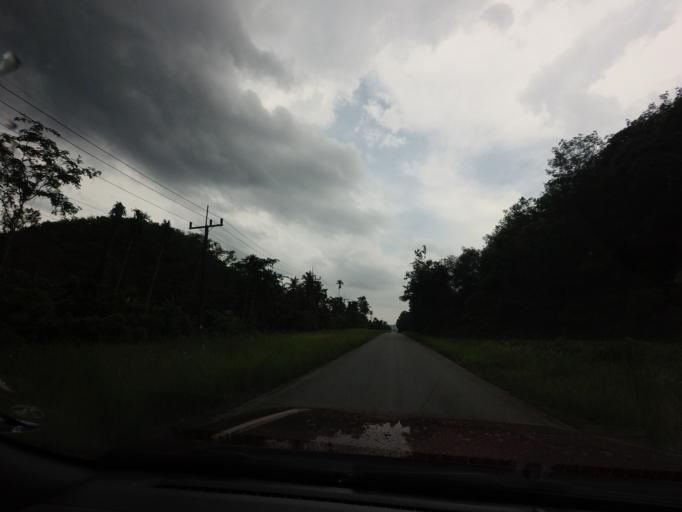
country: TH
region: Yala
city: Ban Nang Sata
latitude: 6.2205
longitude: 101.2299
